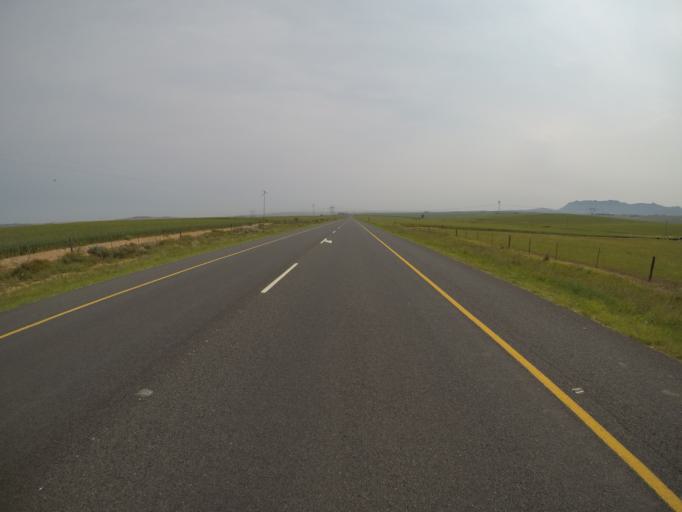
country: ZA
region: Western Cape
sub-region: West Coast District Municipality
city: Malmesbury
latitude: -33.4987
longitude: 18.8322
